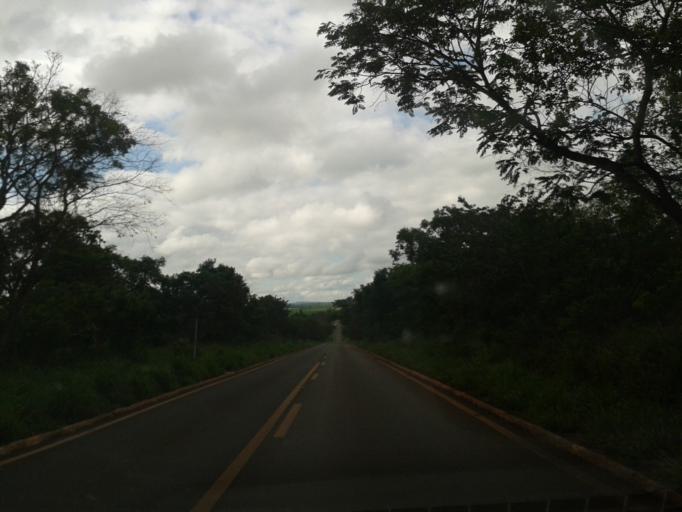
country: BR
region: Minas Gerais
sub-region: Ituiutaba
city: Ituiutaba
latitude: -19.0717
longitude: -49.7661
